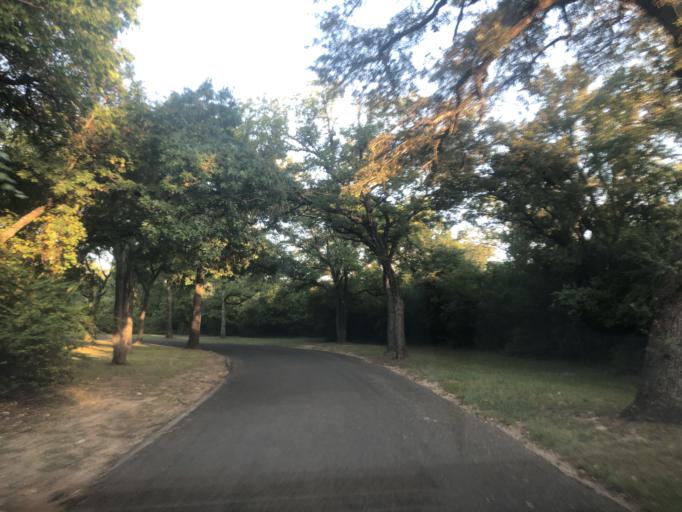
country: US
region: Texas
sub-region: Tarrant County
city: Lakeside
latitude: 32.7977
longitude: -97.4904
